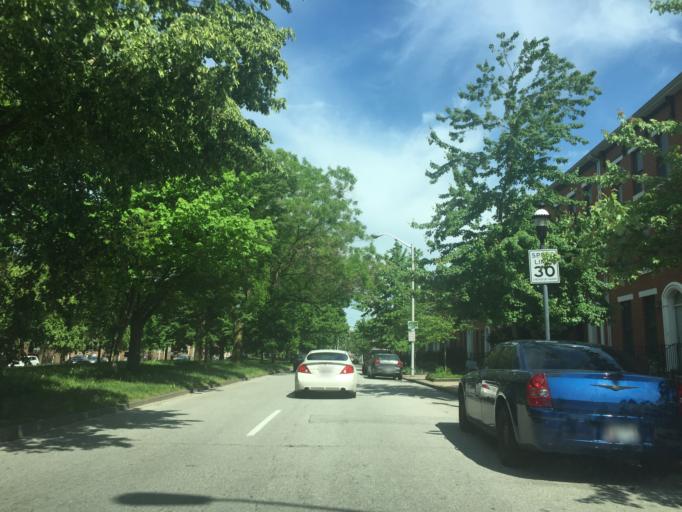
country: US
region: Maryland
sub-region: City of Baltimore
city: Baltimore
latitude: 39.3087
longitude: -76.6318
